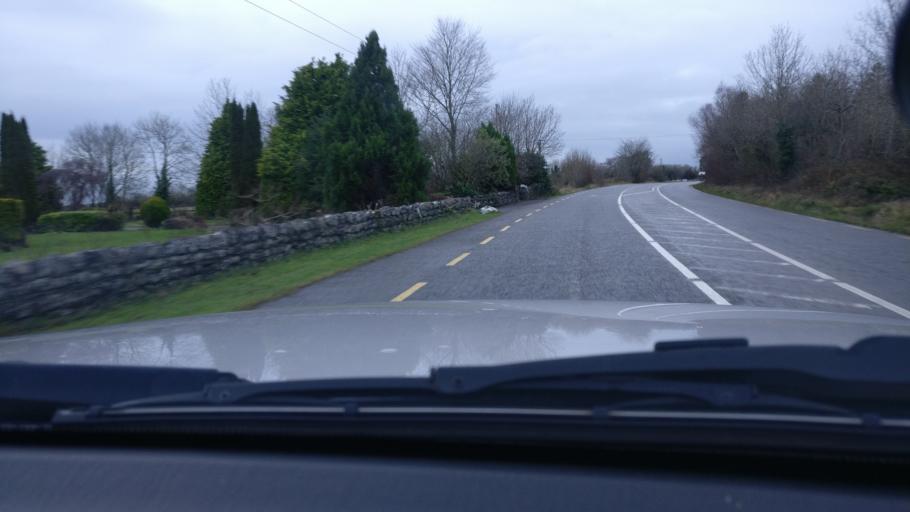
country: IE
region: Leinster
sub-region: An Iarmhi
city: Athlone
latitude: 53.3700
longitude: -8.0231
